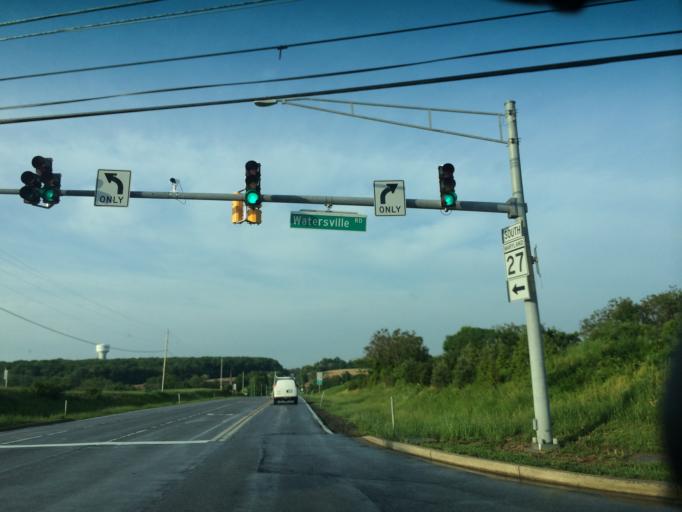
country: US
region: Maryland
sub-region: Carroll County
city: Mount Airy
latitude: 39.3801
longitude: -77.1430
